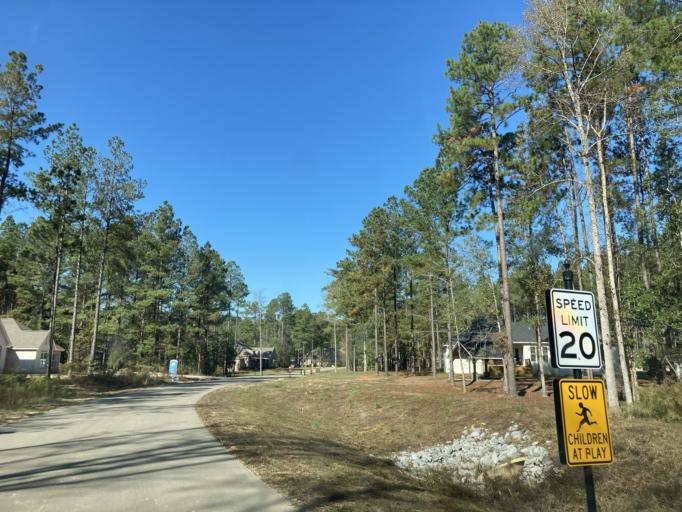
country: US
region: Mississippi
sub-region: Lamar County
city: Sumrall
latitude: 31.3284
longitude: -89.4866
